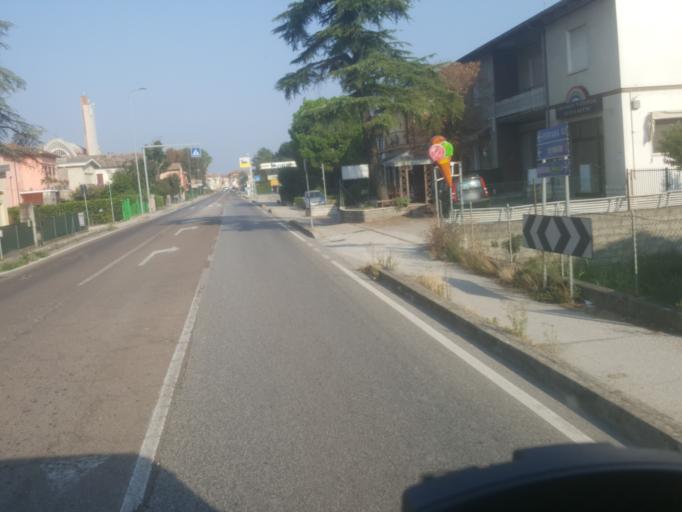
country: IT
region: Emilia-Romagna
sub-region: Provincia di Ravenna
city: Mezzano
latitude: 44.4655
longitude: 12.0891
